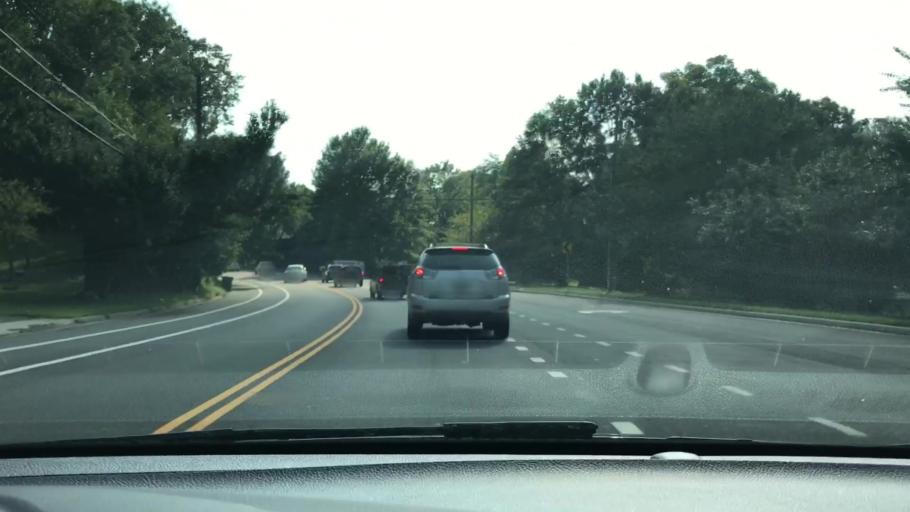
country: US
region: Virginia
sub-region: Fairfax County
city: Jefferson
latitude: 38.8513
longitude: -77.2008
